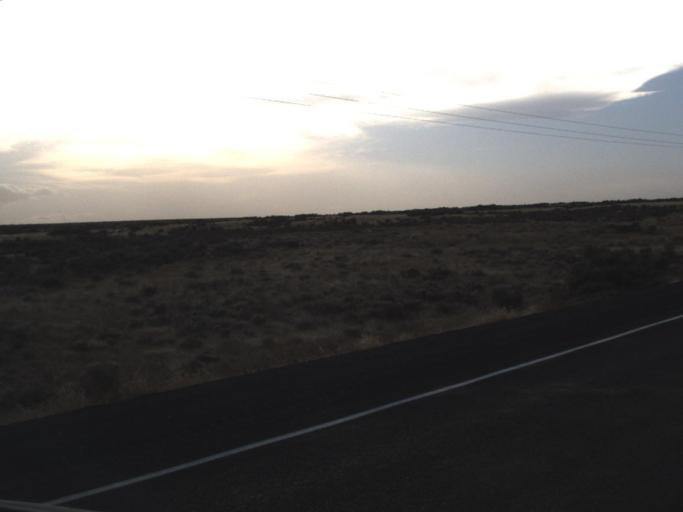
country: US
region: Washington
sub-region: Grant County
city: Warden
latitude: 47.3139
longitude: -118.7852
